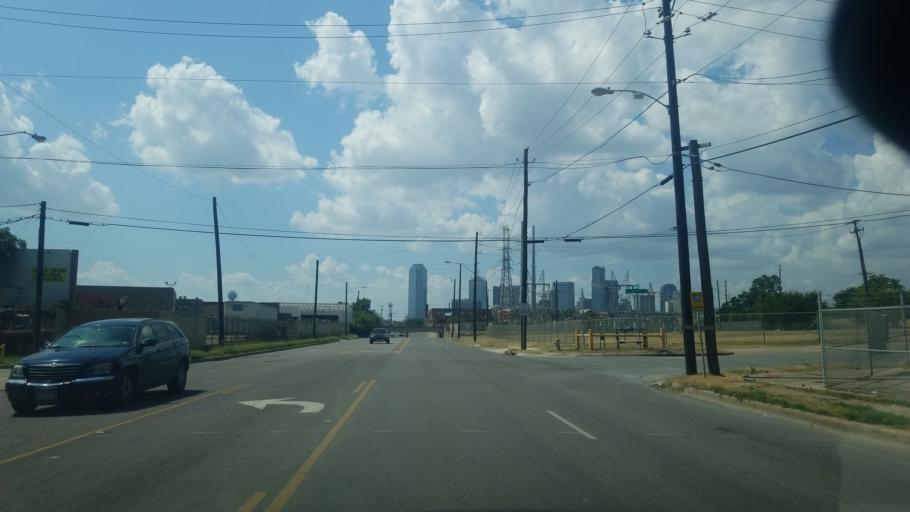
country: US
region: Texas
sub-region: Dallas County
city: Dallas
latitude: 32.7608
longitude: -96.7841
